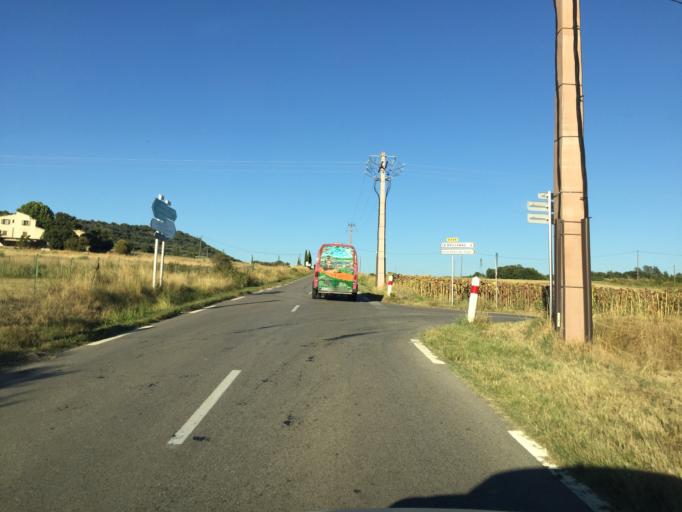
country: FR
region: Provence-Alpes-Cote d'Azur
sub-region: Departement des Alpes-de-Haute-Provence
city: Oraison
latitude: 43.9581
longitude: 5.8701
